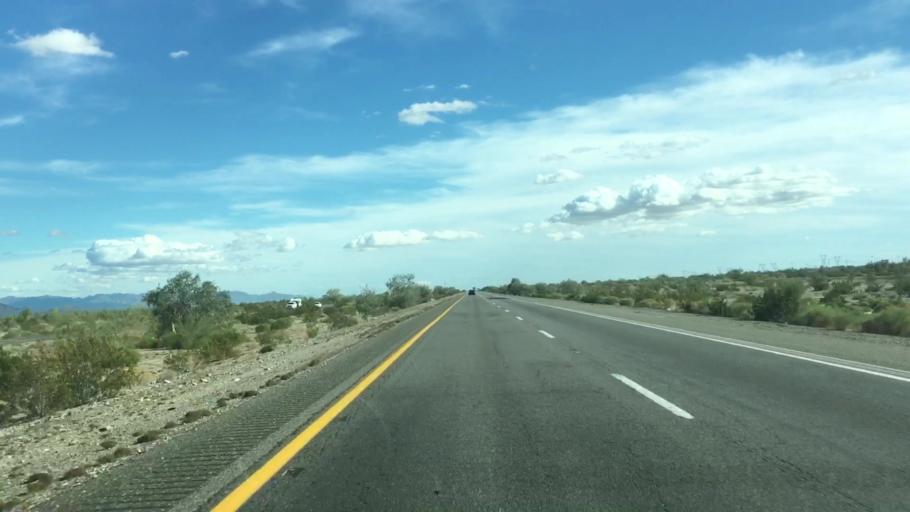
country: US
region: California
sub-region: Imperial County
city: Niland
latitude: 33.6971
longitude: -115.2937
